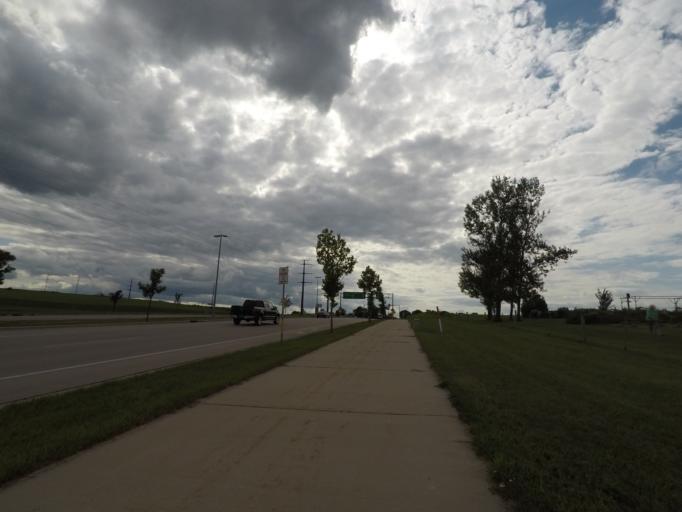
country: US
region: Wisconsin
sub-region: Dane County
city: Middleton
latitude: 43.0605
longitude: -89.5337
